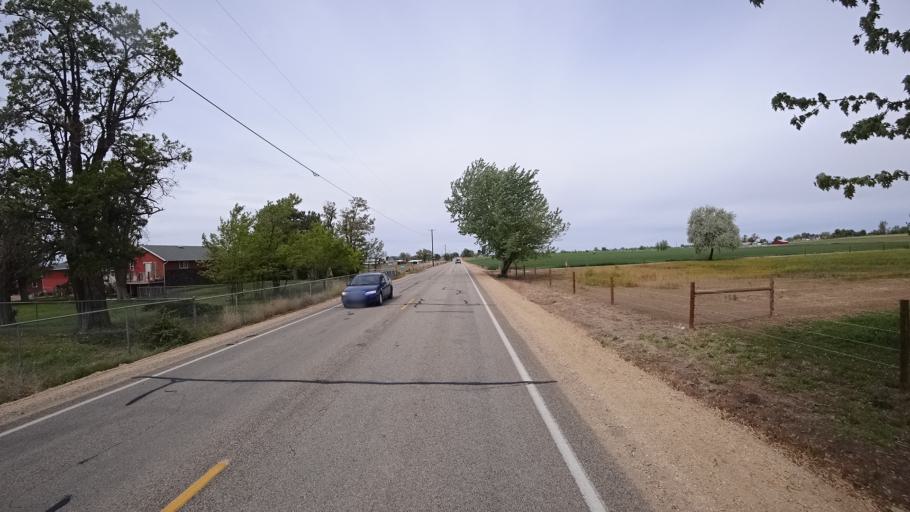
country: US
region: Idaho
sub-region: Ada County
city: Kuna
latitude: 43.5612
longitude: -116.4477
